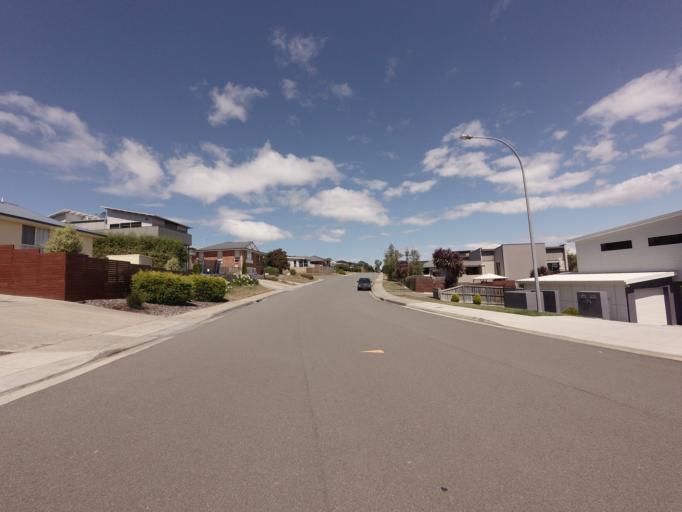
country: AU
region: Tasmania
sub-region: Clarence
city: Rokeby
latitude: -42.9019
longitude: 147.4592
